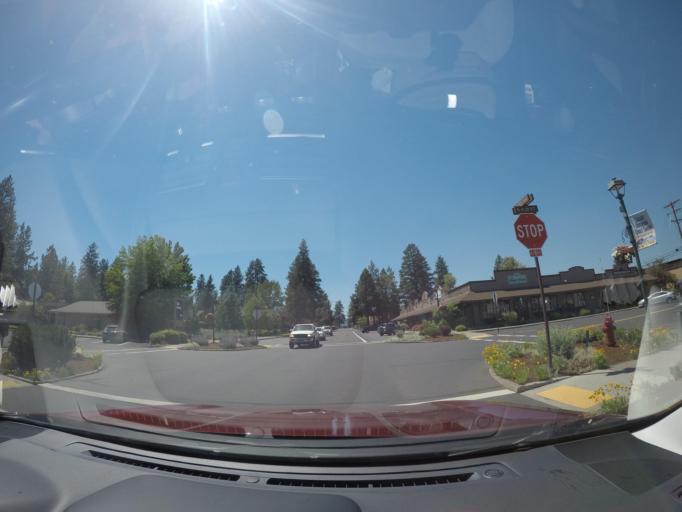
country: US
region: Oregon
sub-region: Deschutes County
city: Sisters
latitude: 44.2905
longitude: -121.5498
